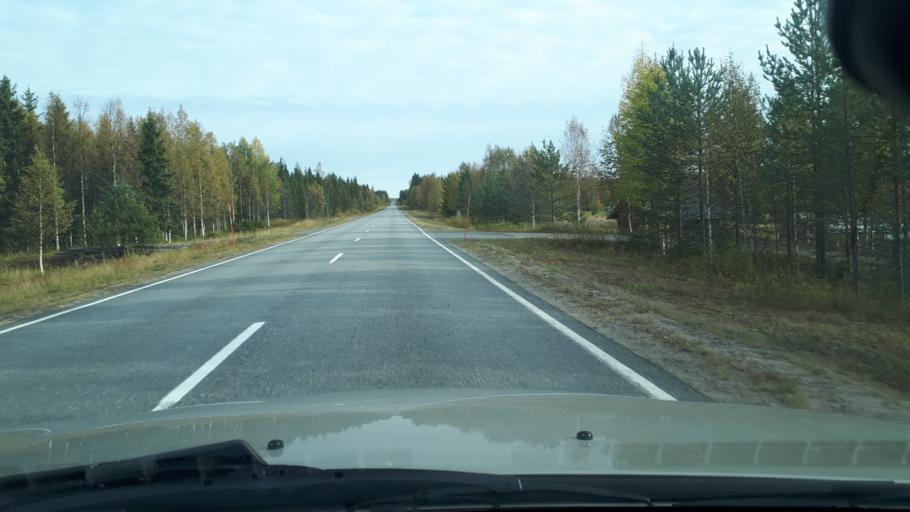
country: FI
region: Lapland
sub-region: Rovaniemi
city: Ranua
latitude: 65.9684
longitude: 26.0926
